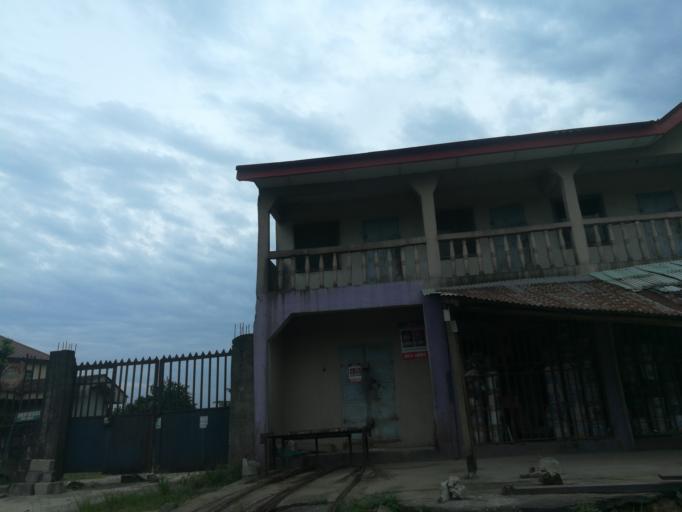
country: NG
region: Rivers
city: Port Harcourt
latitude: 4.7922
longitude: 6.9571
